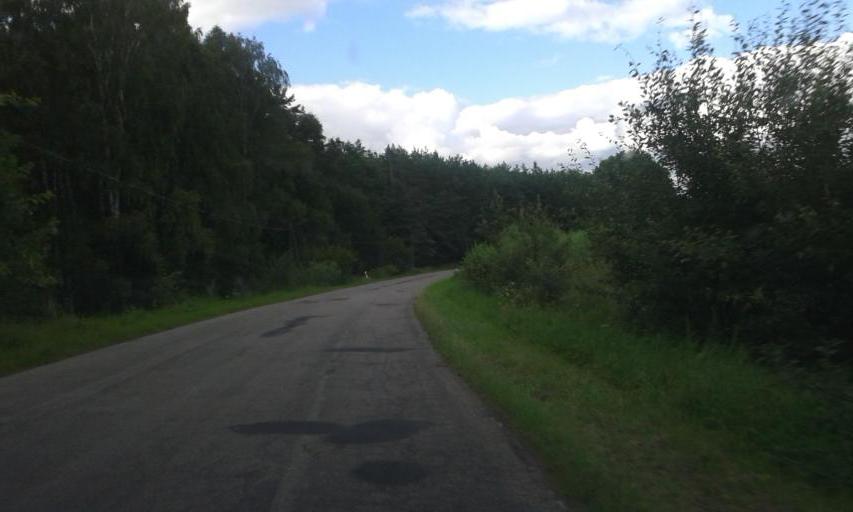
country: PL
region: West Pomeranian Voivodeship
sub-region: Powiat szczecinecki
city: Barwice
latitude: 53.6887
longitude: 16.3430
